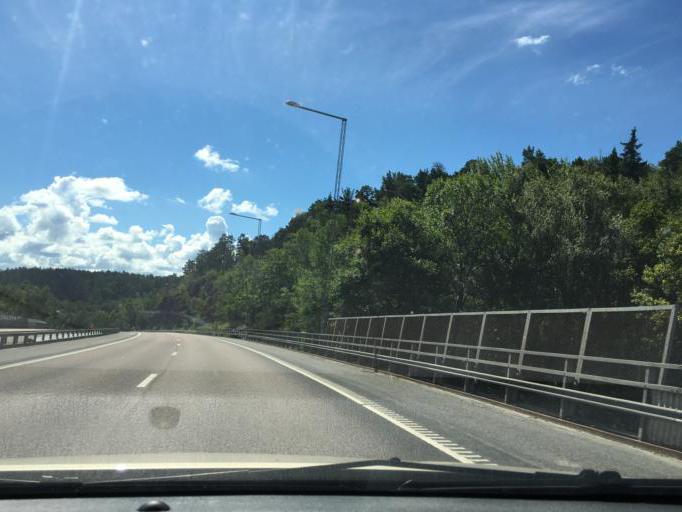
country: SE
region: Stockholm
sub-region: Nacka Kommun
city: Nacka
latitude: 59.3046
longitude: 18.1822
